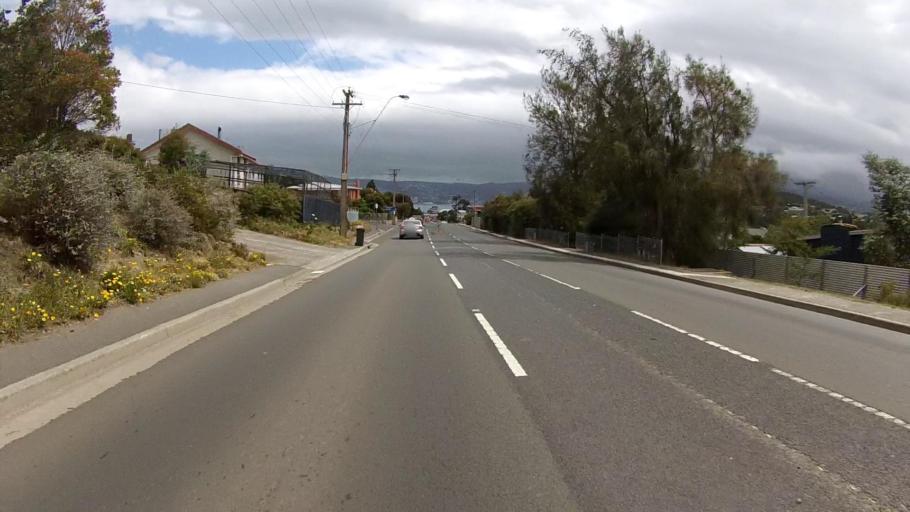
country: AU
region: Tasmania
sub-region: Clarence
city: Bellerive
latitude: -42.8649
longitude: 147.3747
